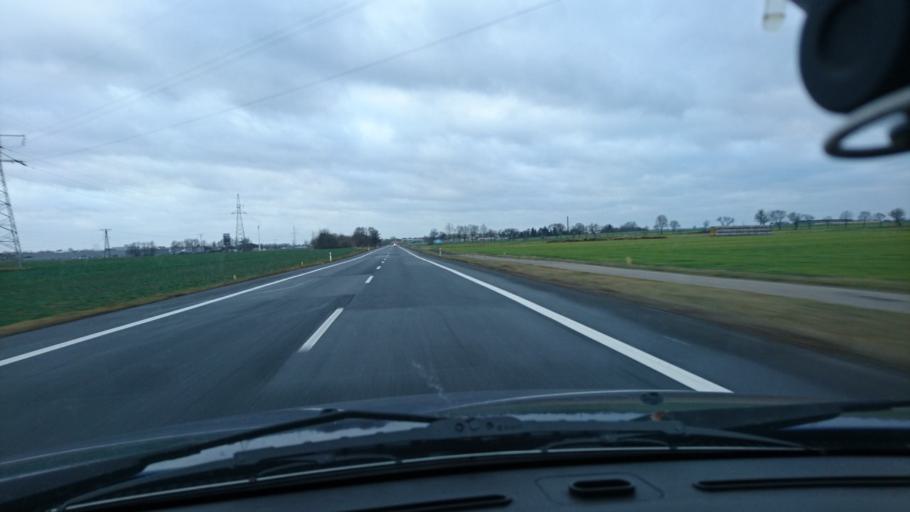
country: PL
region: Opole Voivodeship
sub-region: Powiat kluczborski
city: Kluczbork
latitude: 50.9904
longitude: 18.2239
